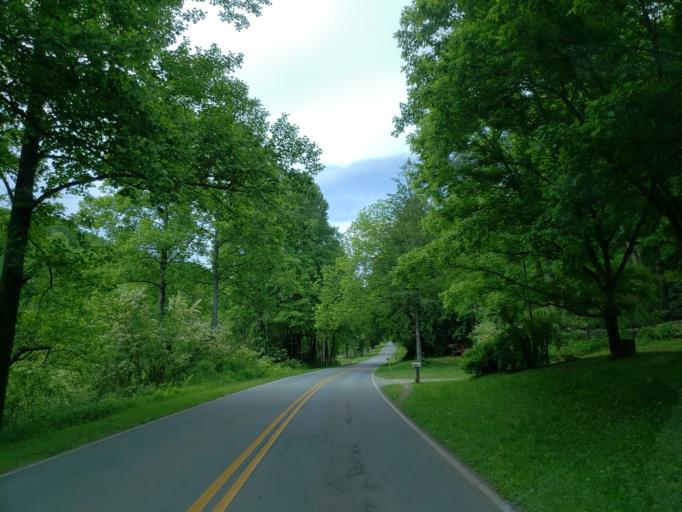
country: US
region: Georgia
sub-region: Fannin County
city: Blue Ridge
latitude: 34.8337
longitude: -84.4039
